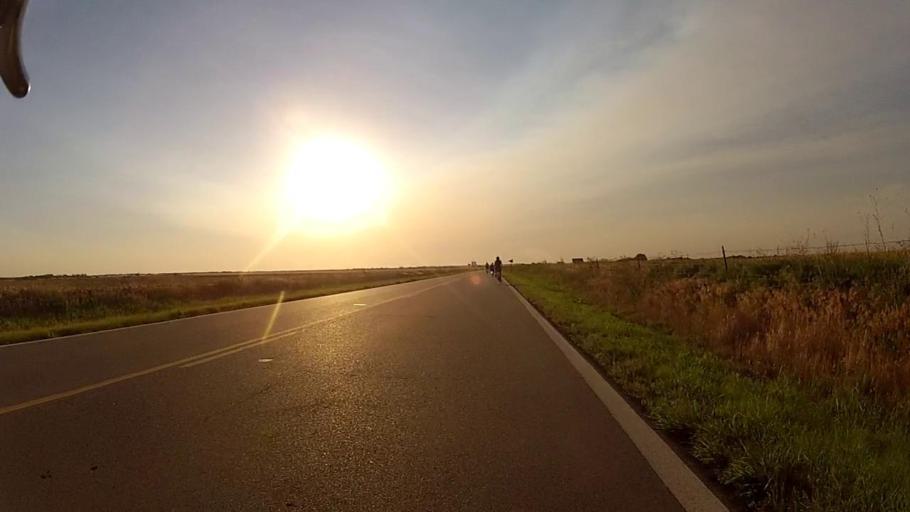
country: US
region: Kansas
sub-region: Harper County
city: Anthony
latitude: 37.1532
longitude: -97.9095
